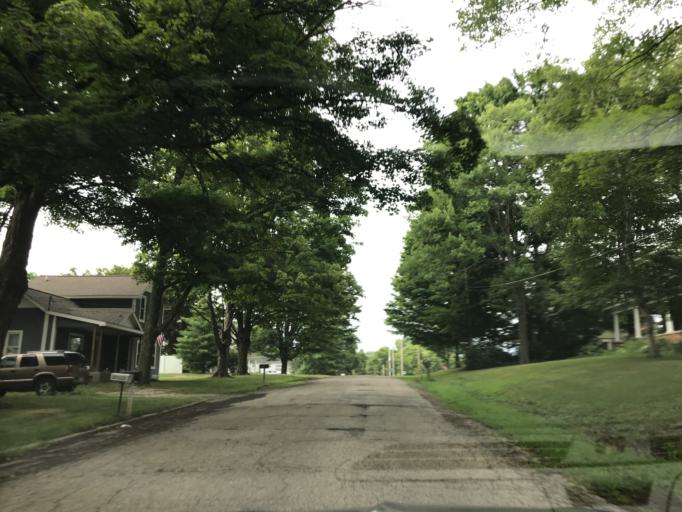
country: US
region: Michigan
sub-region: Jackson County
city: Spring Arbor
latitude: 42.1454
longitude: -84.5164
